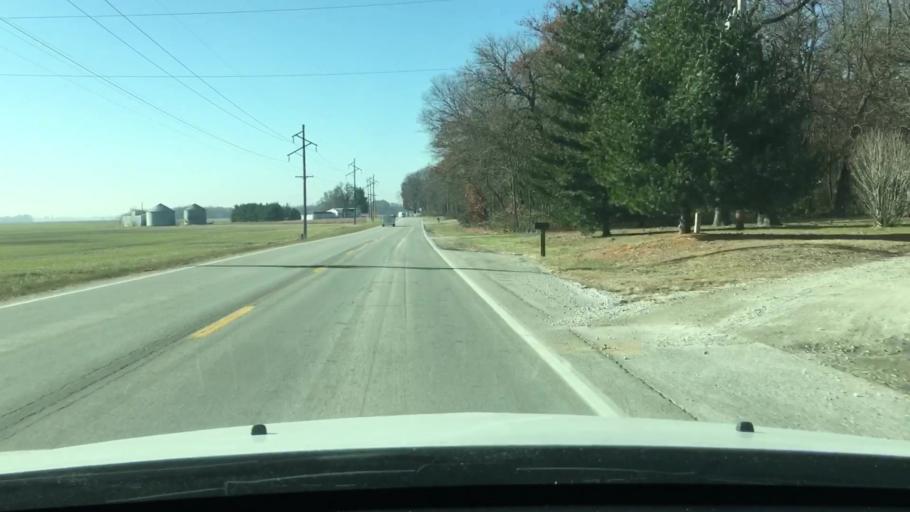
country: US
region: Illinois
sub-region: Cass County
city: Beardstown
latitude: 39.9805
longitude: -90.4519
